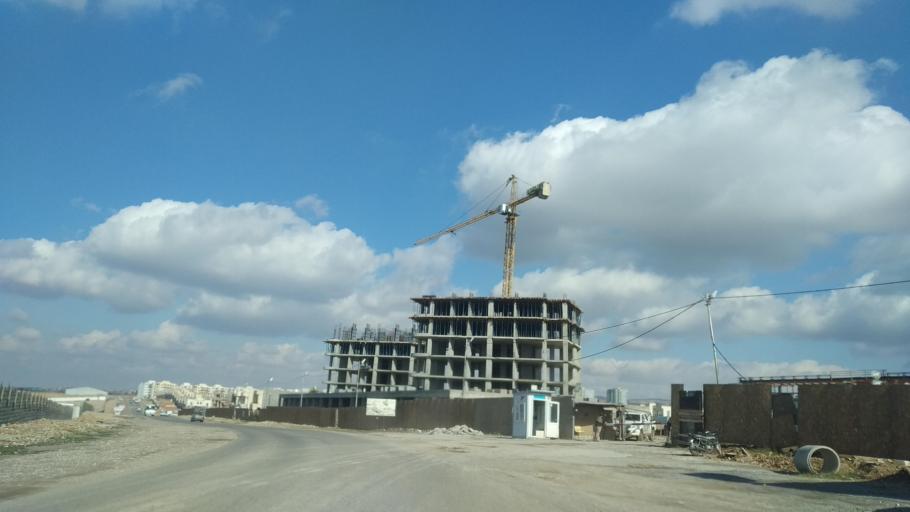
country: IQ
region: Arbil
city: Erbil
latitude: 36.2144
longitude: 44.1376
